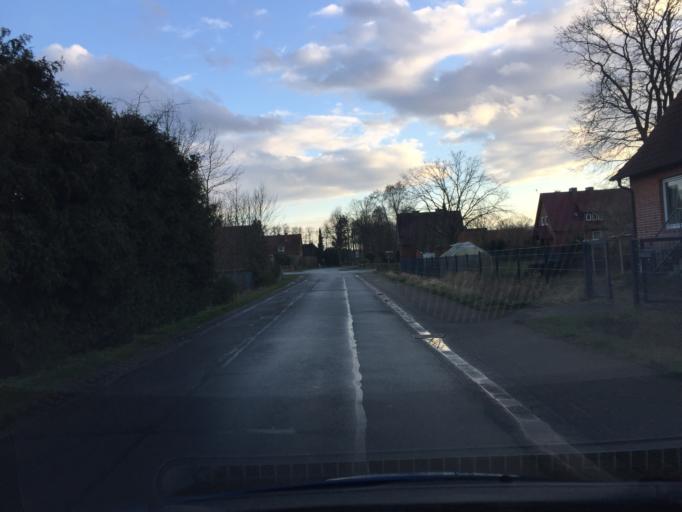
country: DE
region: Lower Saxony
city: Echem
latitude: 53.3372
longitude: 10.5432
